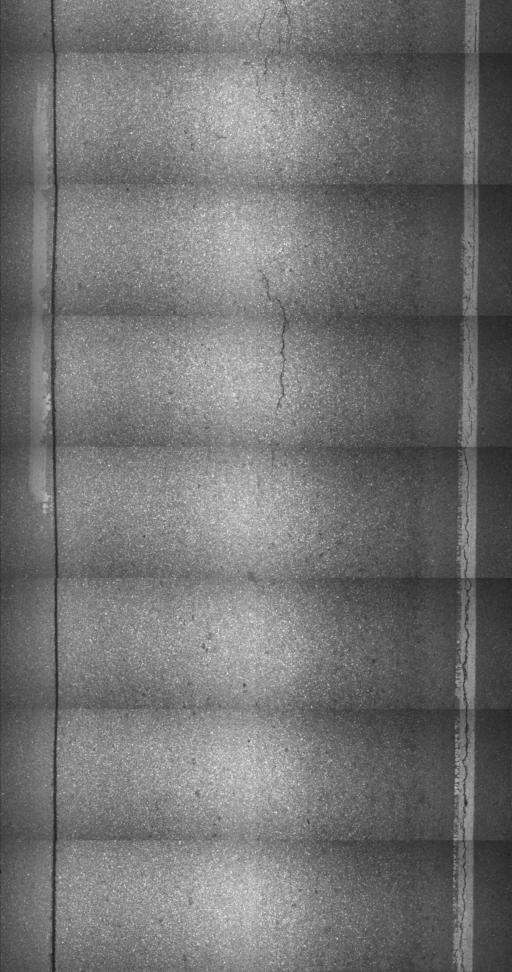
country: US
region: Vermont
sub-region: Orange County
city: Randolph
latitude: 43.9066
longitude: -72.8289
